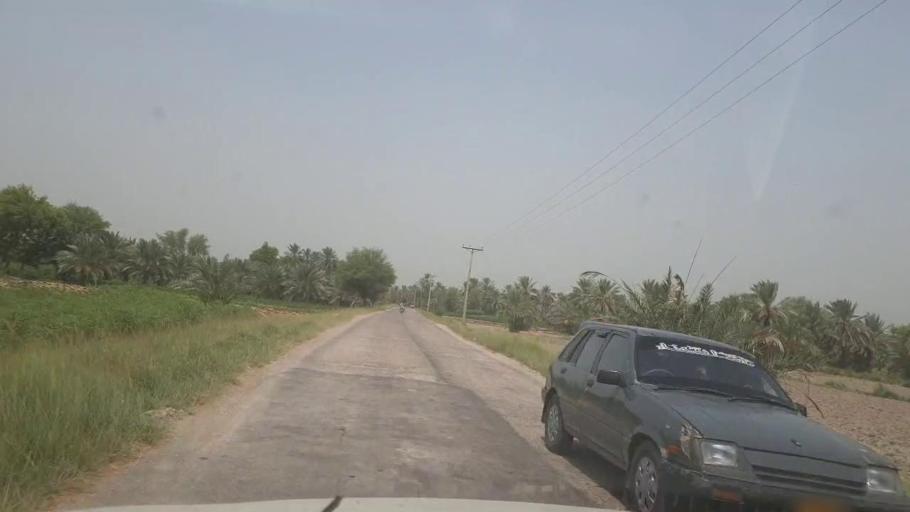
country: PK
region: Sindh
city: Kot Diji
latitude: 27.3624
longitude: 68.6815
